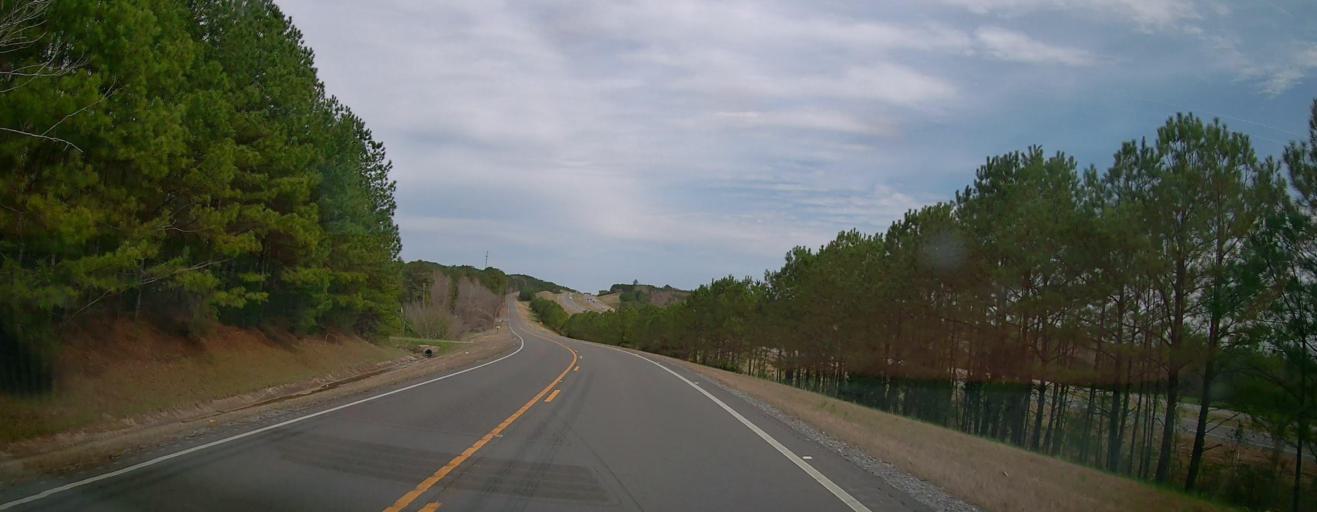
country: US
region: Alabama
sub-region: Walker County
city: Carbon Hill
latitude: 33.8645
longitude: -87.4079
